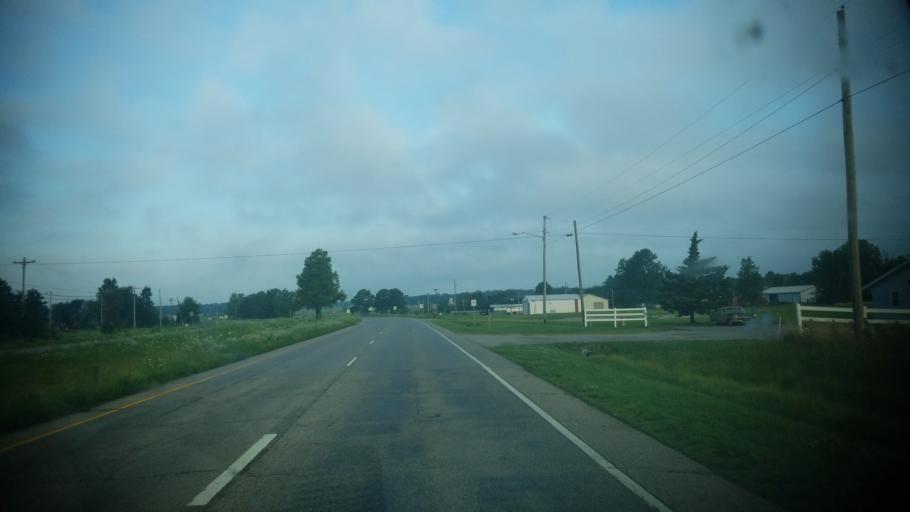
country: US
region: Illinois
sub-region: Wayne County
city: Fairfield
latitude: 38.3797
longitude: -88.3982
